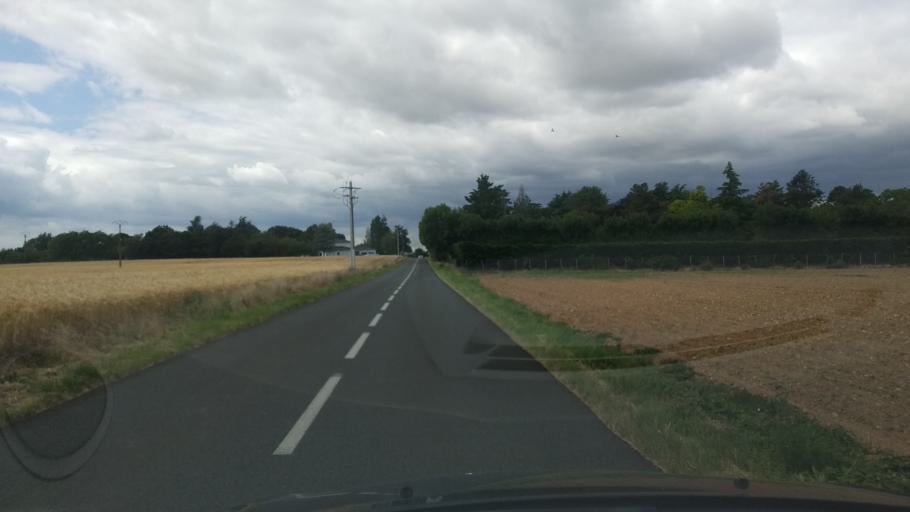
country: FR
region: Poitou-Charentes
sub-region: Departement de la Vienne
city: Vouille
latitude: 46.6274
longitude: 0.1945
